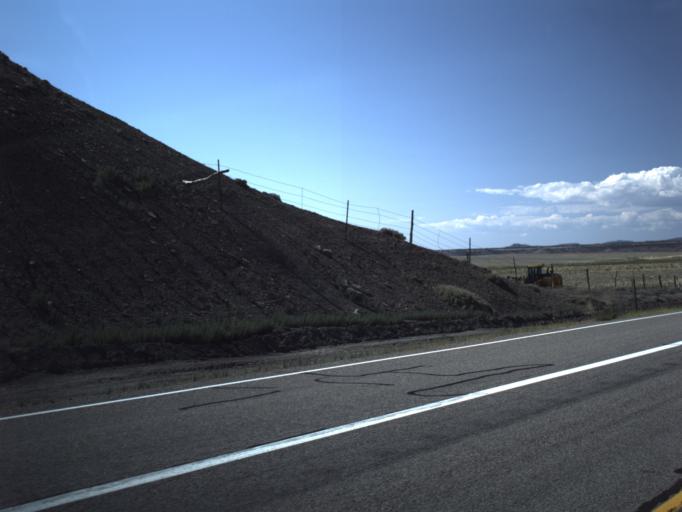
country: US
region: Utah
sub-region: Emery County
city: Ferron
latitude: 38.8511
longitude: -111.3078
